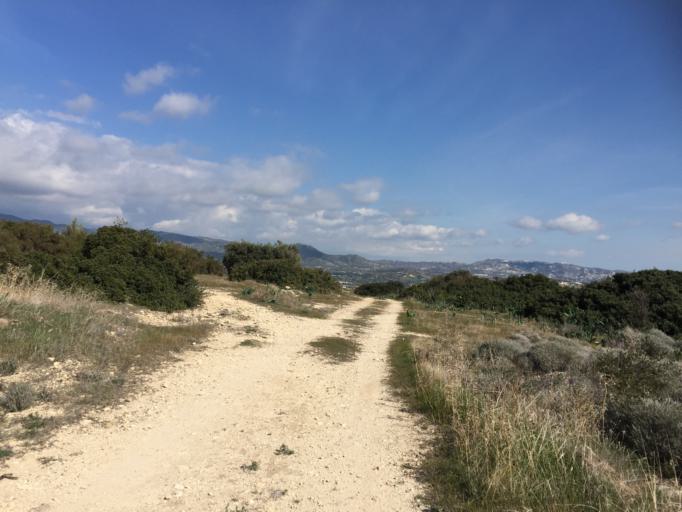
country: CY
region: Larnaka
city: Agios Tychon
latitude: 34.7371
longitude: 33.1411
